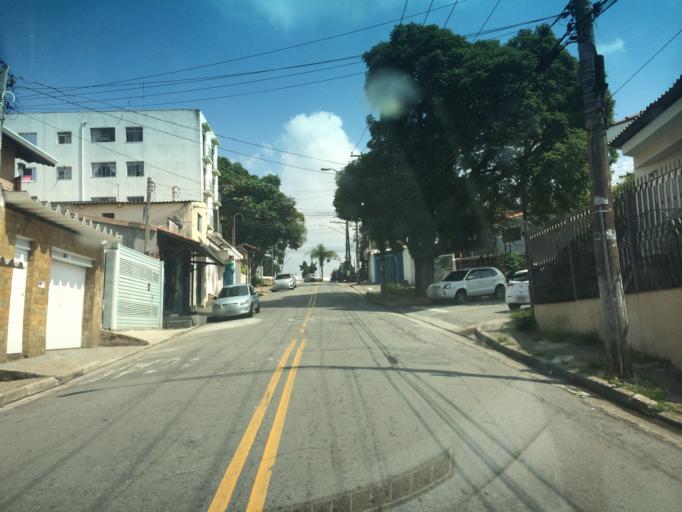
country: BR
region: Sao Paulo
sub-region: Guarulhos
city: Guarulhos
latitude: -23.4537
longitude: -46.5389
